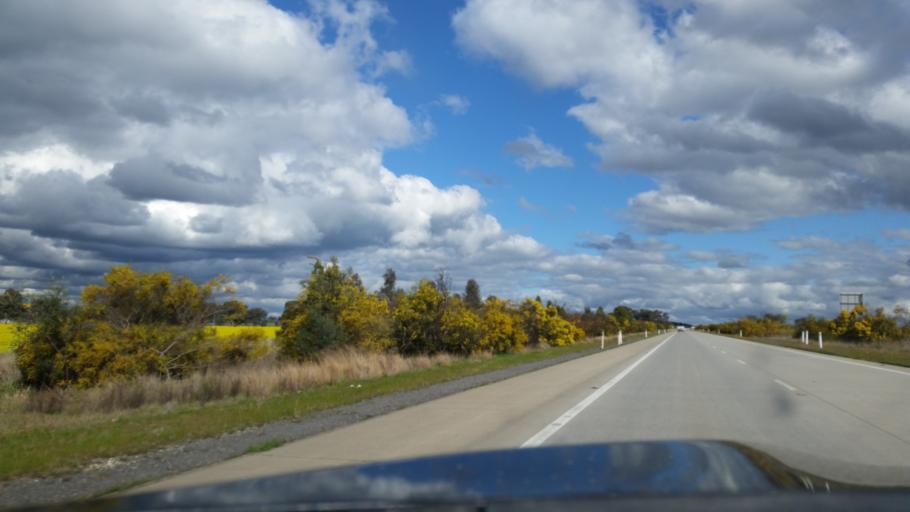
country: AU
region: New South Wales
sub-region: Greater Hume Shire
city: Jindera
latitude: -35.9463
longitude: 147.0039
